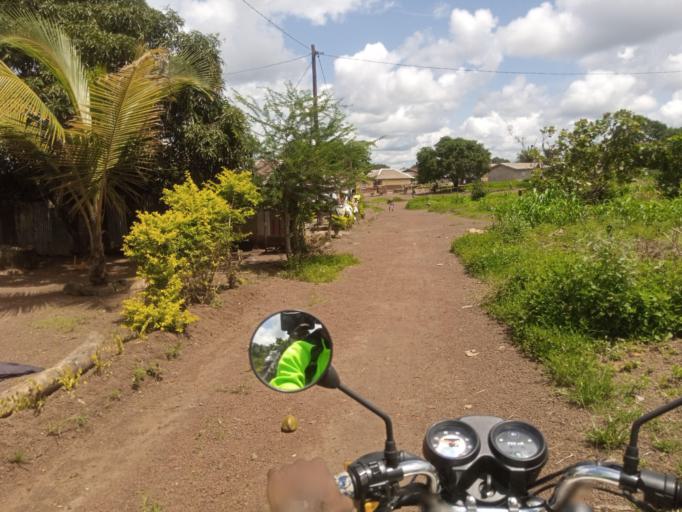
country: SL
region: Northern Province
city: Port Loko
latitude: 8.7591
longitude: -12.7819
